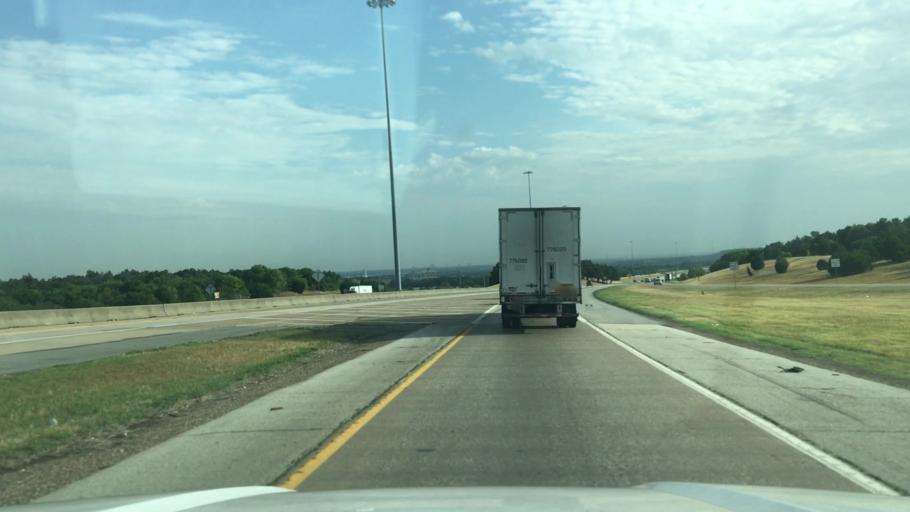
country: US
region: Texas
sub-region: Dallas County
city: Duncanville
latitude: 32.6749
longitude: -96.9463
